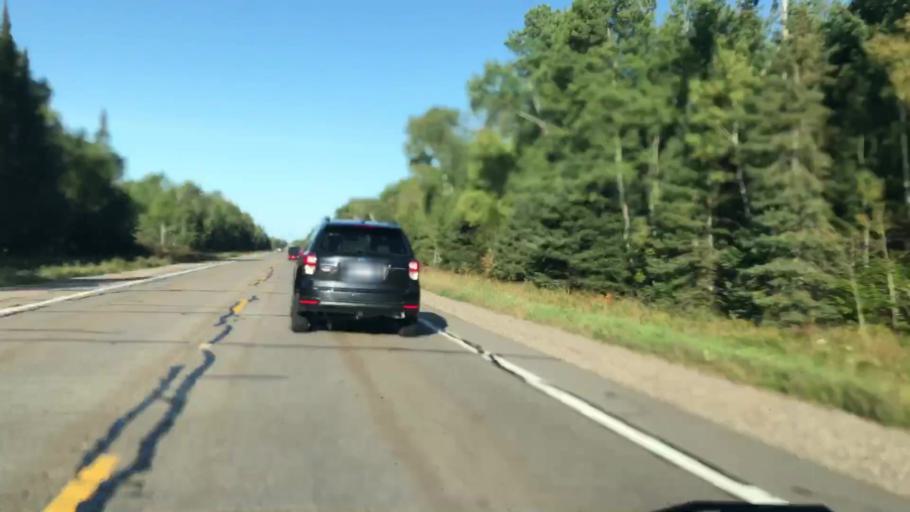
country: US
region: Michigan
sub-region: Chippewa County
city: Sault Ste. Marie
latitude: 46.3759
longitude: -84.6401
